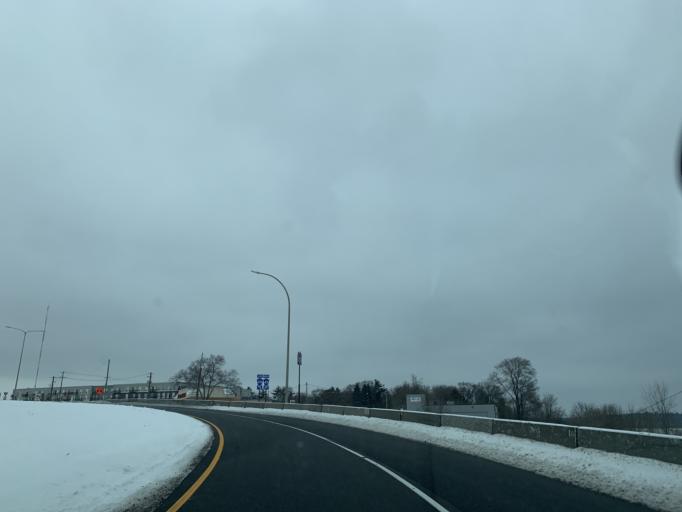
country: US
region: Minnesota
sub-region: Ramsey County
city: Little Canada
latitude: 45.0452
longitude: -93.1047
